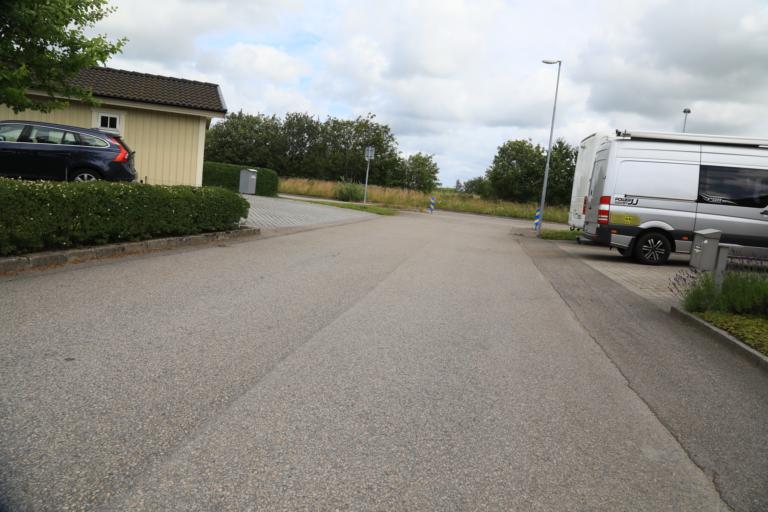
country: SE
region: Halland
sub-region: Varbergs Kommun
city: Traslovslage
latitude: 57.1114
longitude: 12.3008
